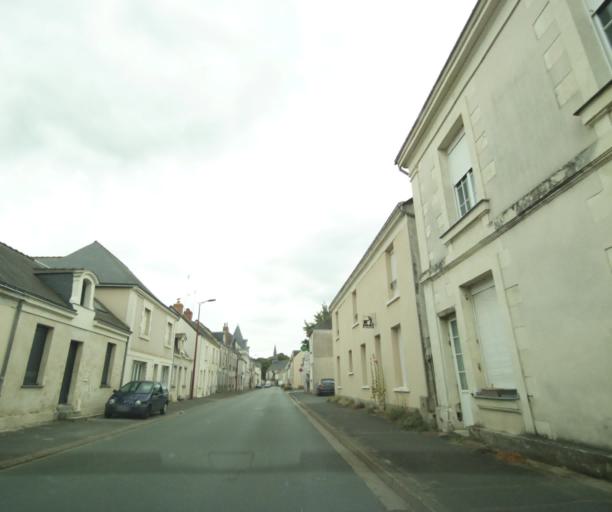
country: FR
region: Pays de la Loire
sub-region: Departement de Maine-et-Loire
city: Pellouailles-les-Vignes
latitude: 47.5218
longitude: -0.4399
